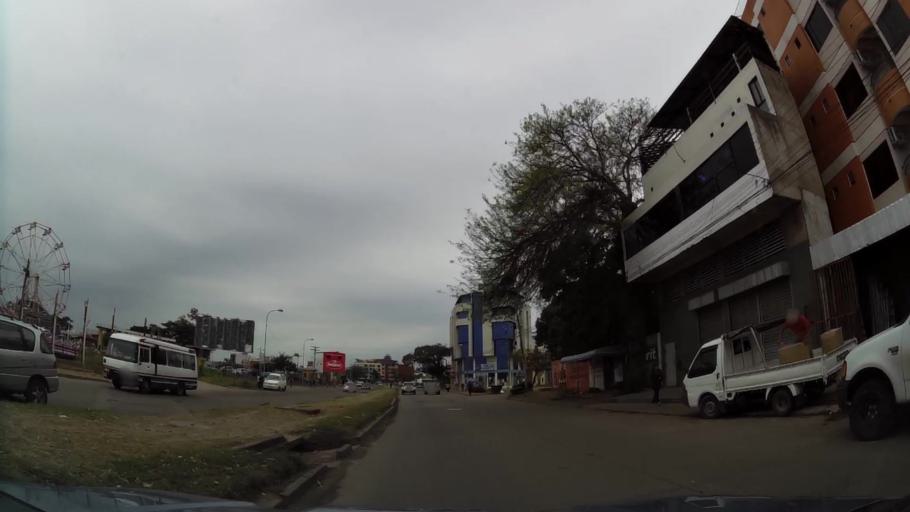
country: BO
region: Santa Cruz
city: Santa Cruz de la Sierra
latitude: -17.7861
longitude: -63.1605
